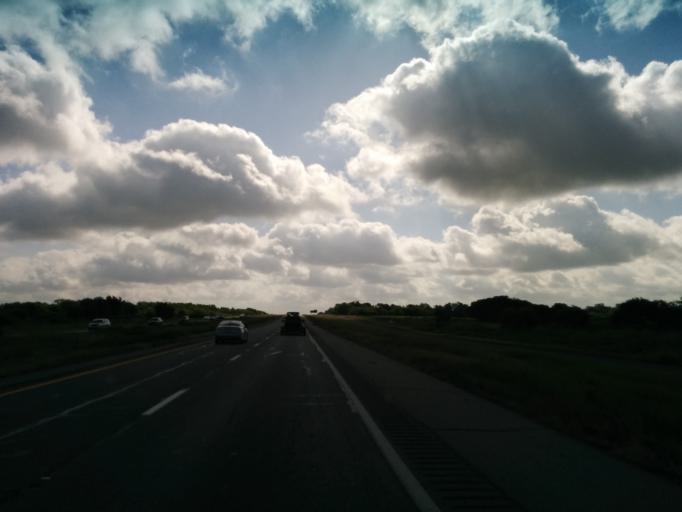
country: US
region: Texas
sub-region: Caldwell County
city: Luling
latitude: 29.6380
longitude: -97.7225
